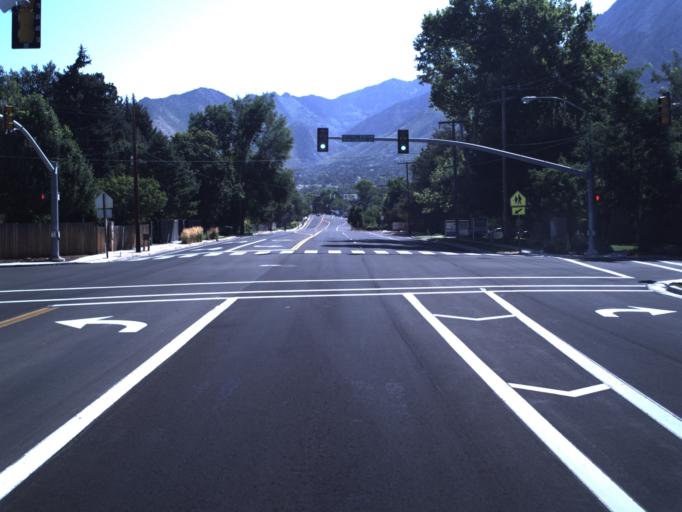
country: US
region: Utah
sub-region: Salt Lake County
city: Holladay
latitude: 40.6742
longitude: -111.8301
